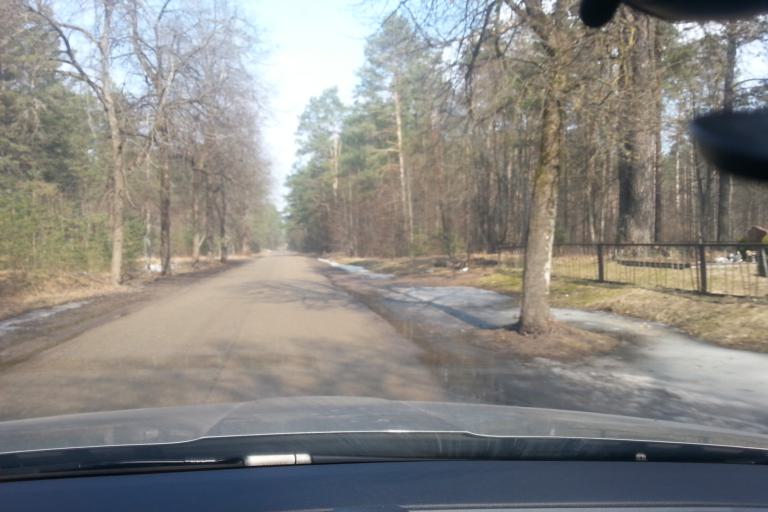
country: LT
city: Trakai
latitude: 54.5057
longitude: 24.9845
